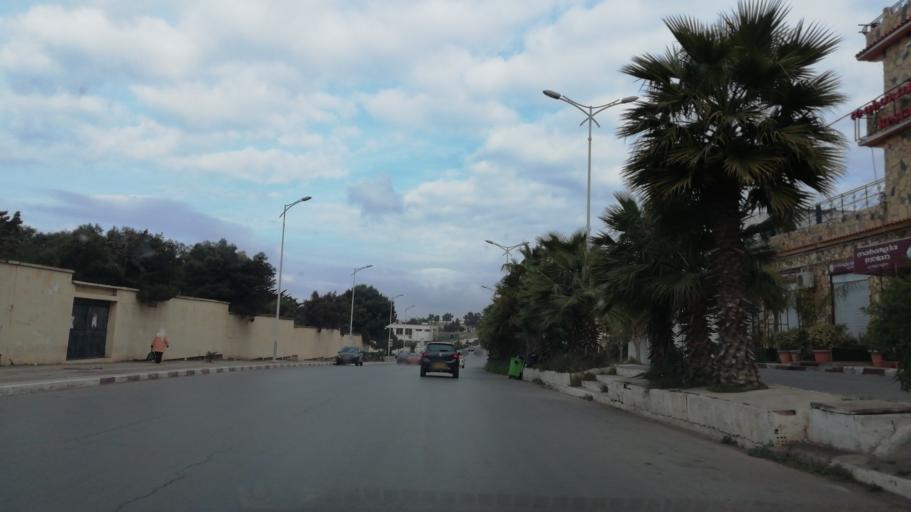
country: DZ
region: Oran
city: Oran
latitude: 35.7126
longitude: -0.6119
